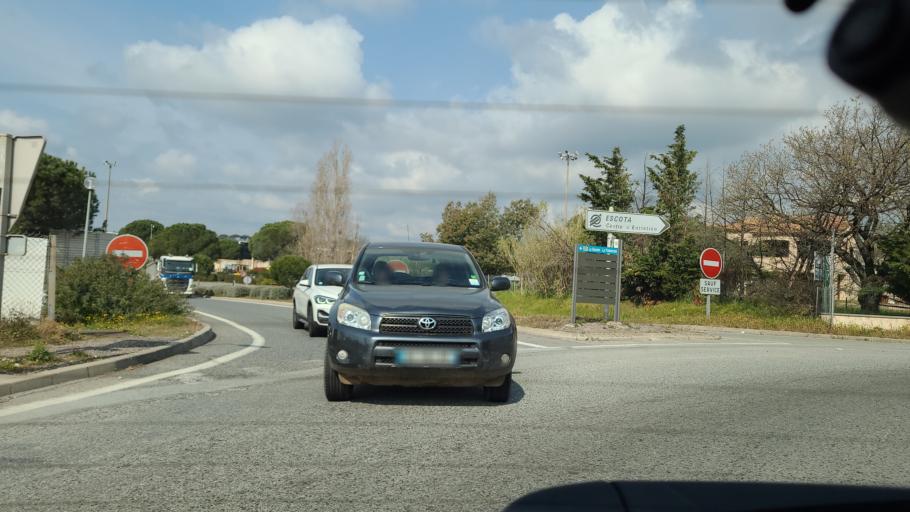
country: FR
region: Provence-Alpes-Cote d'Azur
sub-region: Departement du Var
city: Frejus
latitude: 43.4681
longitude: 6.7328
